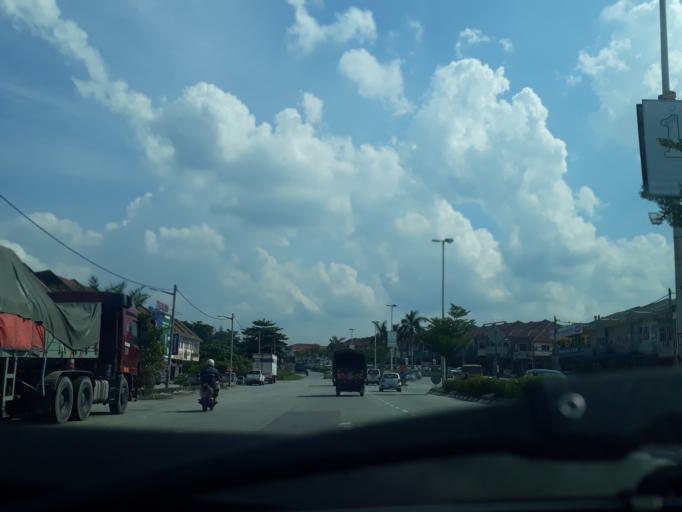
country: MY
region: Perak
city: Ipoh
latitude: 4.6412
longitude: 101.0947
